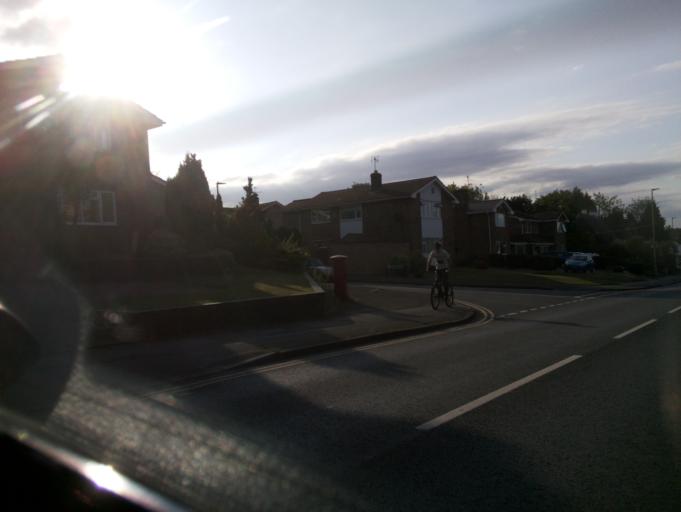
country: GB
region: England
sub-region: Gloucestershire
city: Barnwood
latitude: 51.8458
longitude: -2.2209
